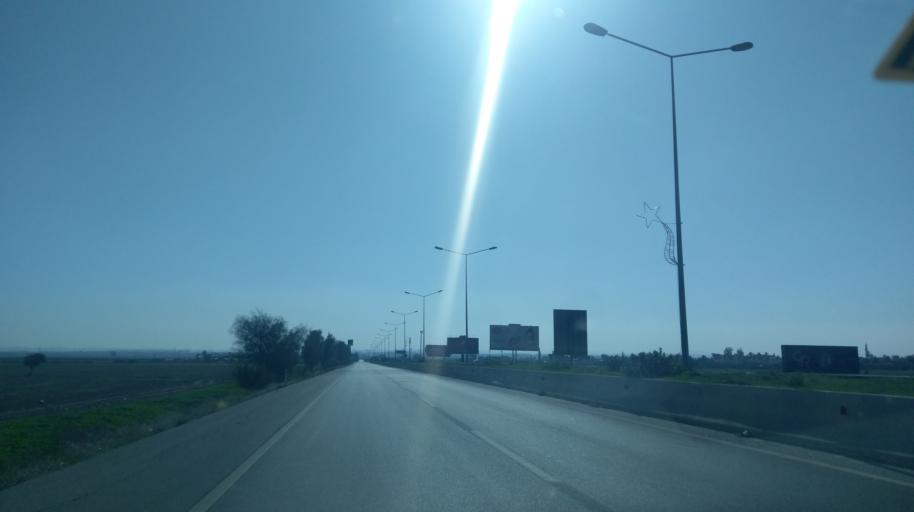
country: CY
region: Lefkosia
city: Geri
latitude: 35.2141
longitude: 33.4979
